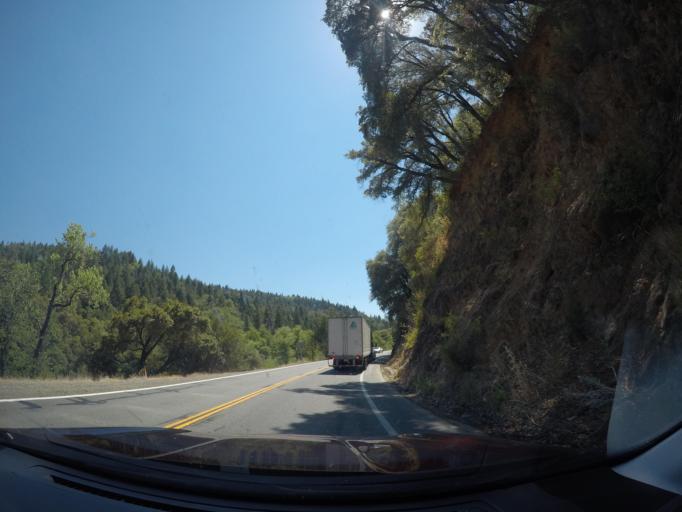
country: US
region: California
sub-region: Shasta County
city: Bella Vista
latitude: 40.7451
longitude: -122.0632
